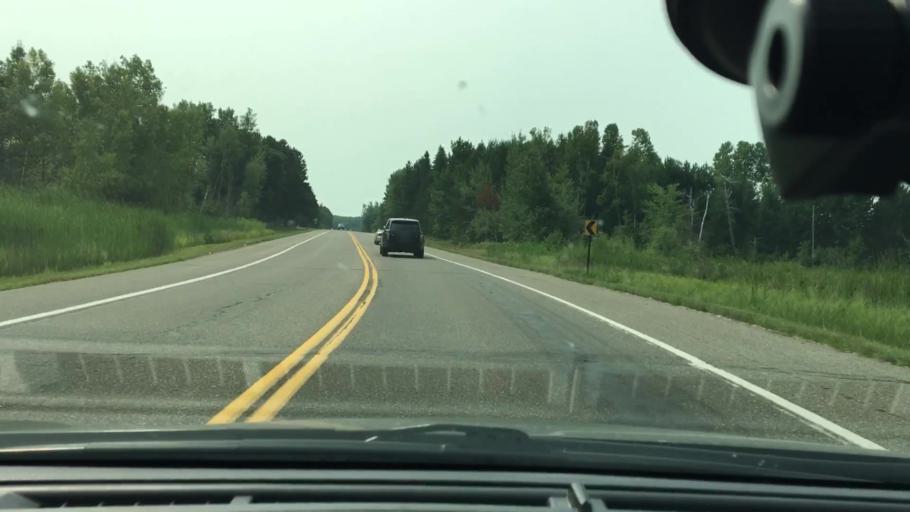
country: US
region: Minnesota
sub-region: Crow Wing County
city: Brainerd
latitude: 46.3965
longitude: -94.2234
